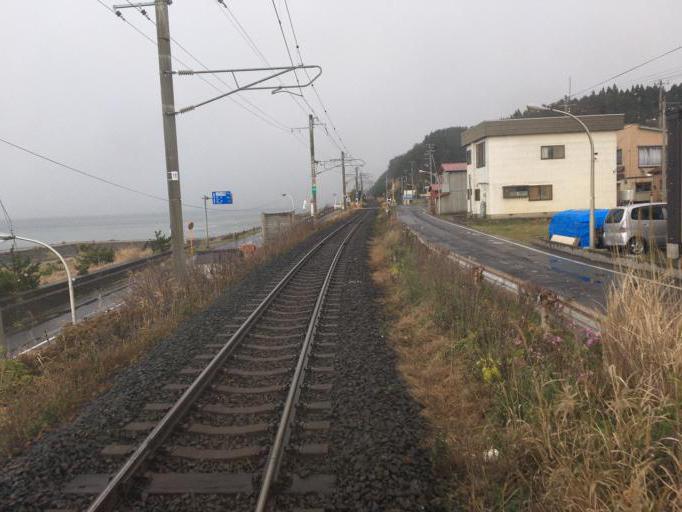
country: JP
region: Aomori
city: Aomori Shi
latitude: 41.0344
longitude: 140.6458
